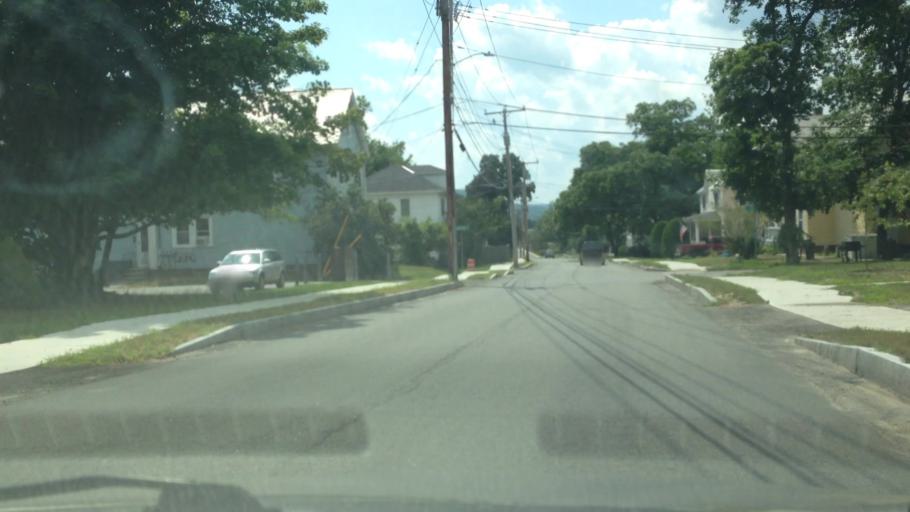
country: US
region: New Hampshire
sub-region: Cheshire County
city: Keene
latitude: 42.9309
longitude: -72.2655
